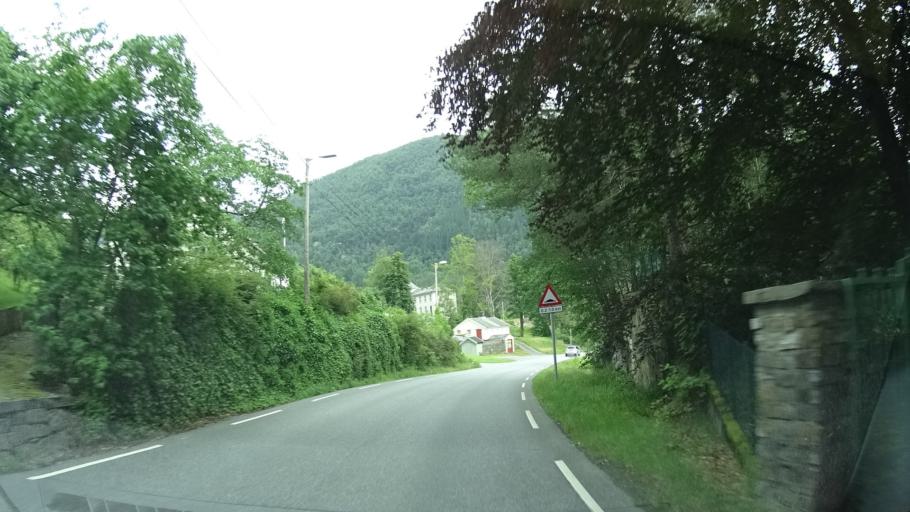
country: NO
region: Hordaland
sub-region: Jondal
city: Jondal
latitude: 60.2816
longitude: 6.2499
